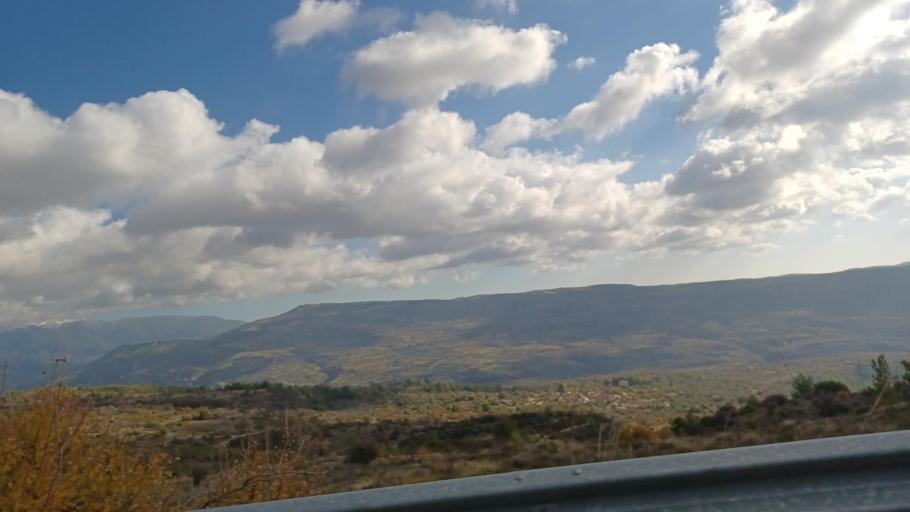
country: CY
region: Limassol
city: Pachna
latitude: 34.8511
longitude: 32.6951
